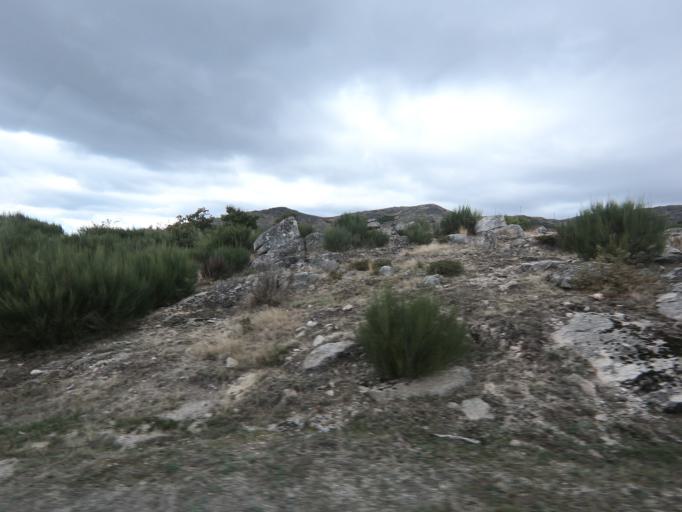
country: PT
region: Vila Real
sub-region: Vila Real
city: Vila Real
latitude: 41.3803
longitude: -7.8101
